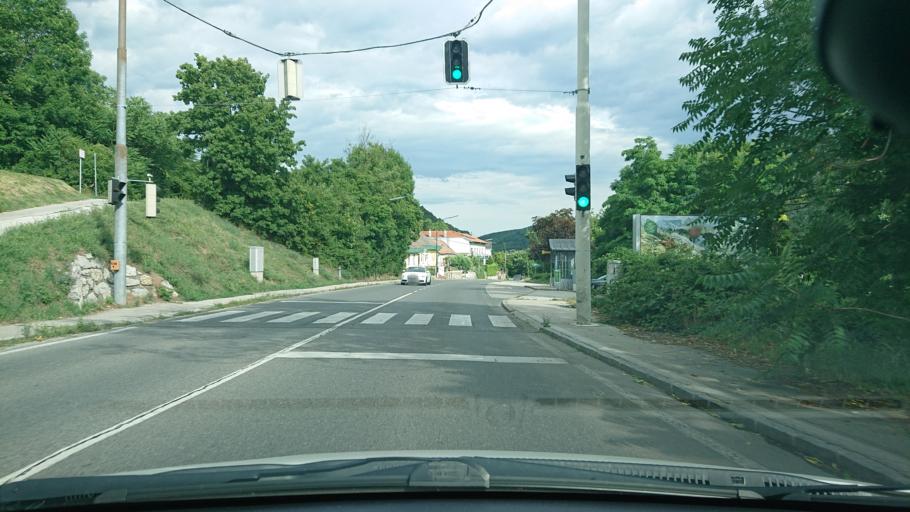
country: AT
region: Lower Austria
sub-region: Politischer Bezirk Baden
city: Berndorf
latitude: 47.9436
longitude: 16.1313
